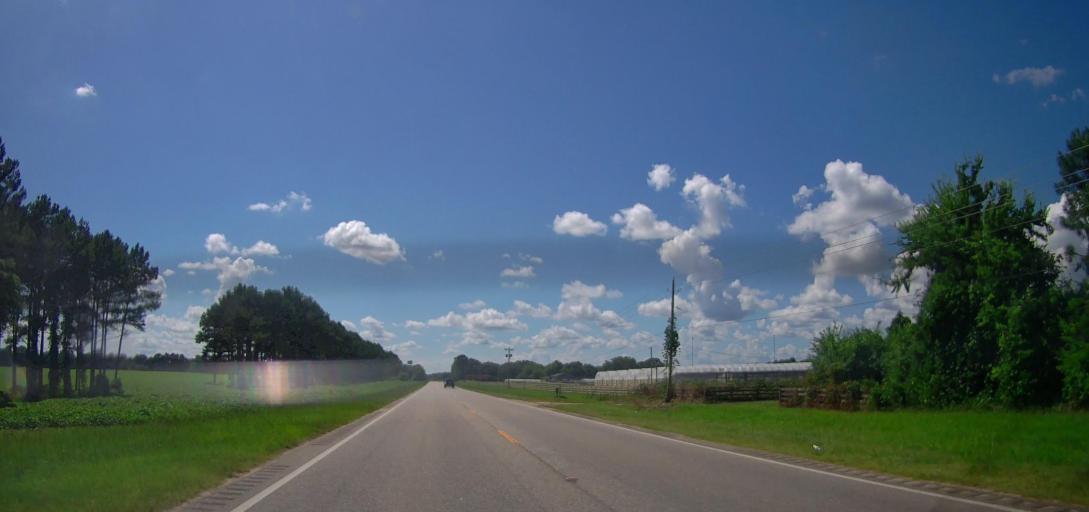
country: US
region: Alabama
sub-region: Elmore County
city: Tallassee
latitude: 32.3899
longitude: -85.8937
